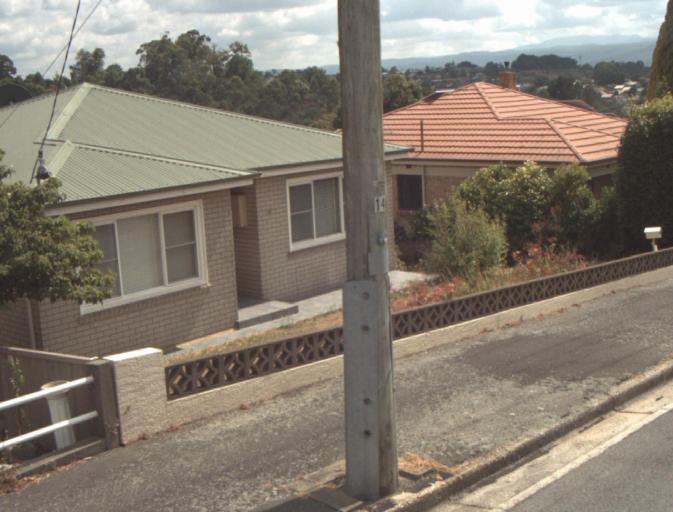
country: AU
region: Tasmania
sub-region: Launceston
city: Summerhill
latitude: -41.4673
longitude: 147.1528
